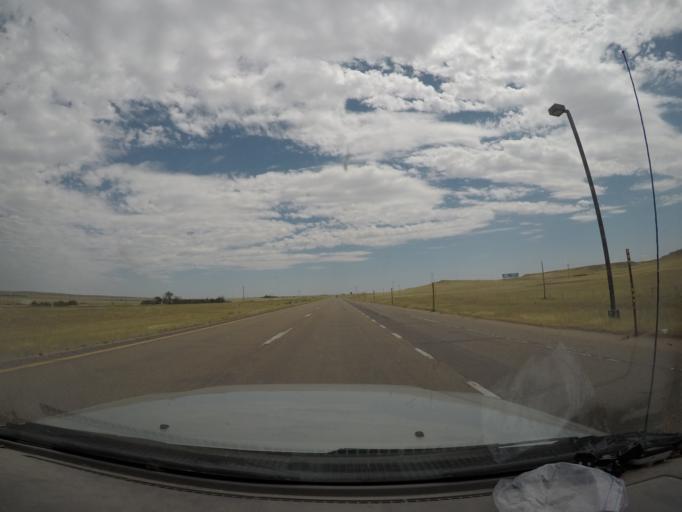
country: US
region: Nebraska
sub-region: Cheyenne County
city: Sidney
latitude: 41.1529
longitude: -103.0833
